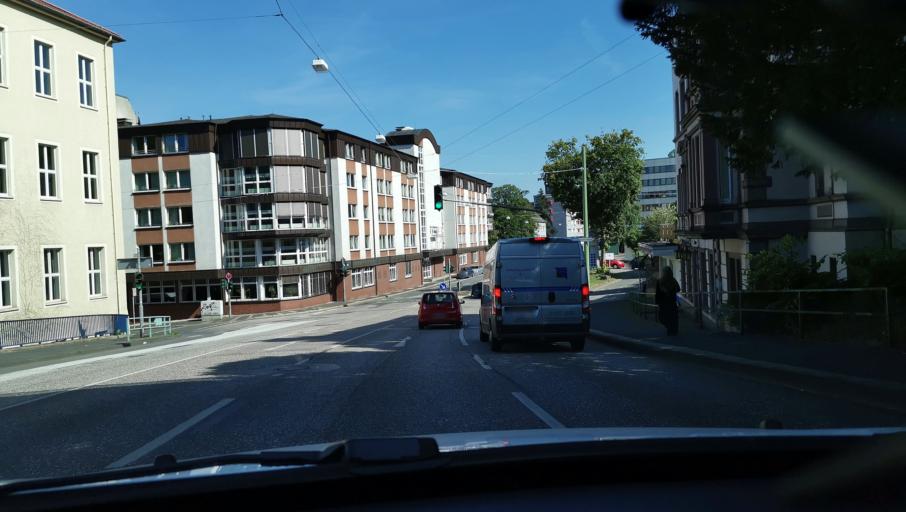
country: DE
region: North Rhine-Westphalia
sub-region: Regierungsbezirk Arnsberg
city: Hagen
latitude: 51.3557
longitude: 7.4688
